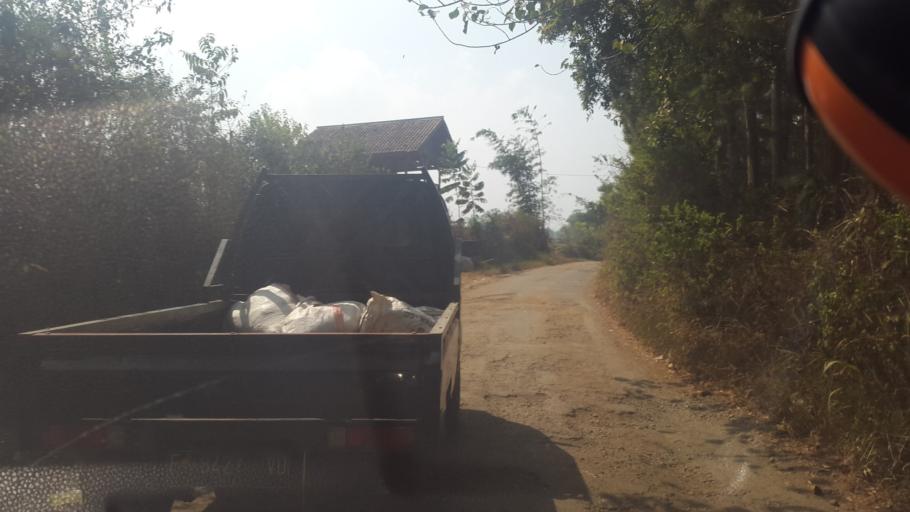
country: ID
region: West Java
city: Pasirlaja
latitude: -7.0545
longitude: 106.8770
